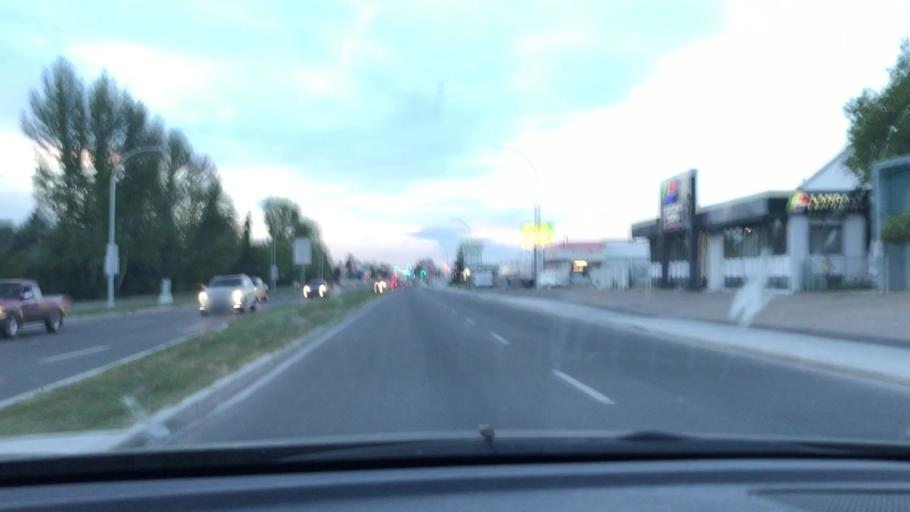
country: CA
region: Alberta
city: Edmonton
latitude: 53.5009
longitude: -113.4573
